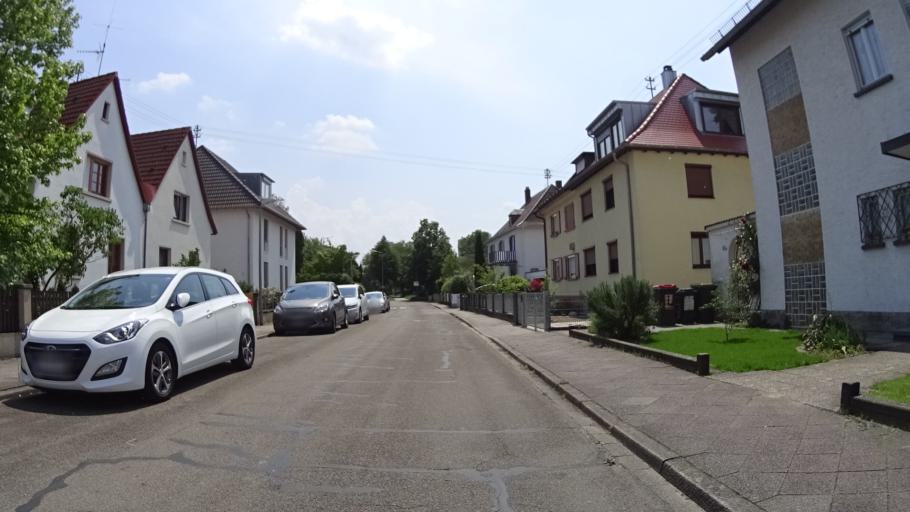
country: DE
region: Baden-Wuerttemberg
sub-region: Karlsruhe Region
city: Rheinstetten
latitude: 49.0020
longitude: 8.3324
